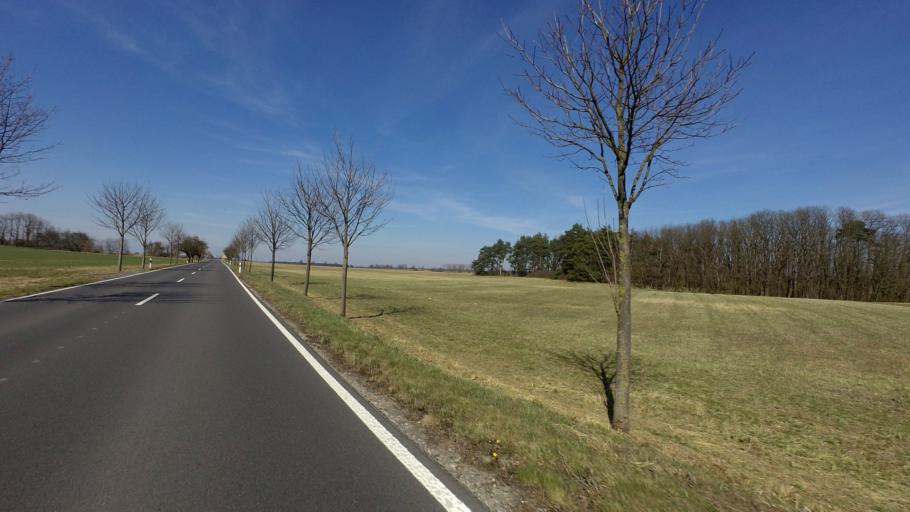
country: DE
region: Brandenburg
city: Waldsieversdorf
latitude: 52.5746
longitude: 14.0328
